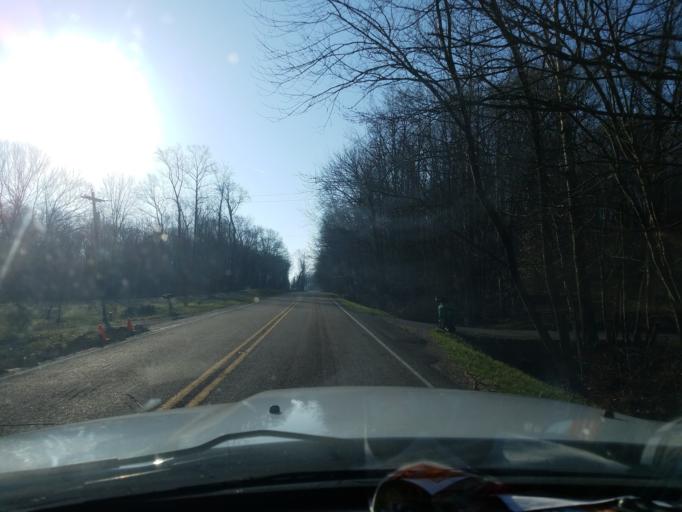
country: US
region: Indiana
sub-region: Owen County
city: Spencer
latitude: 39.3448
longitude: -86.9111
